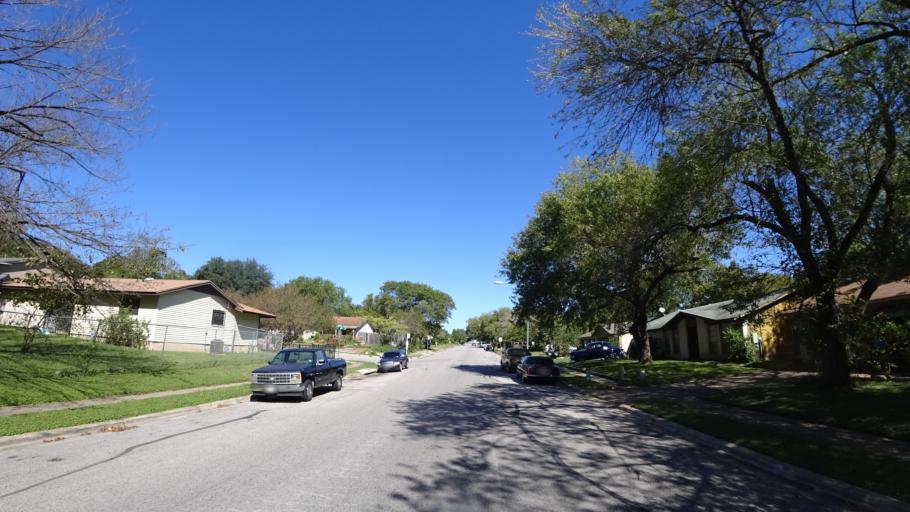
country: US
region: Texas
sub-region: Travis County
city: Austin
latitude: 30.2816
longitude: -97.6605
